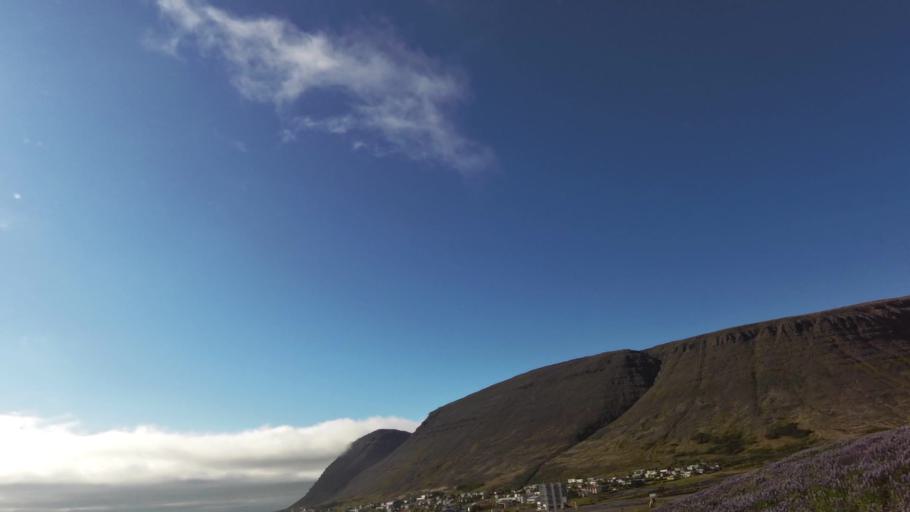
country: IS
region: West
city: Olafsvik
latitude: 65.5867
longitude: -23.9698
